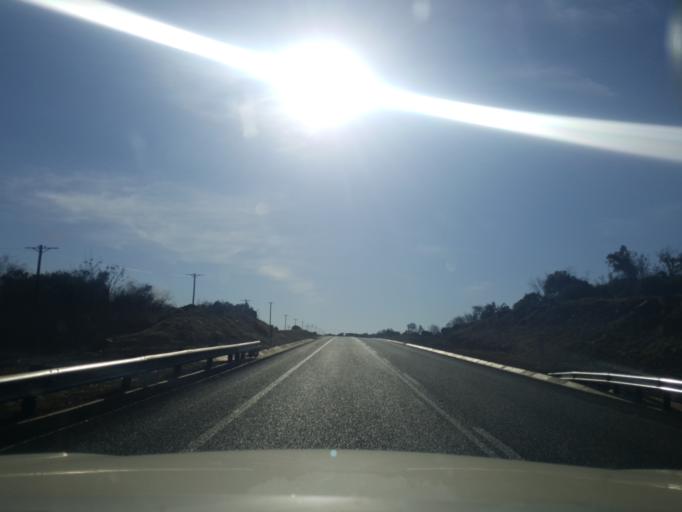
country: ZA
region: North-West
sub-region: Ngaka Modiri Molema District Municipality
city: Zeerust
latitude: -25.5441
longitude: 26.0473
